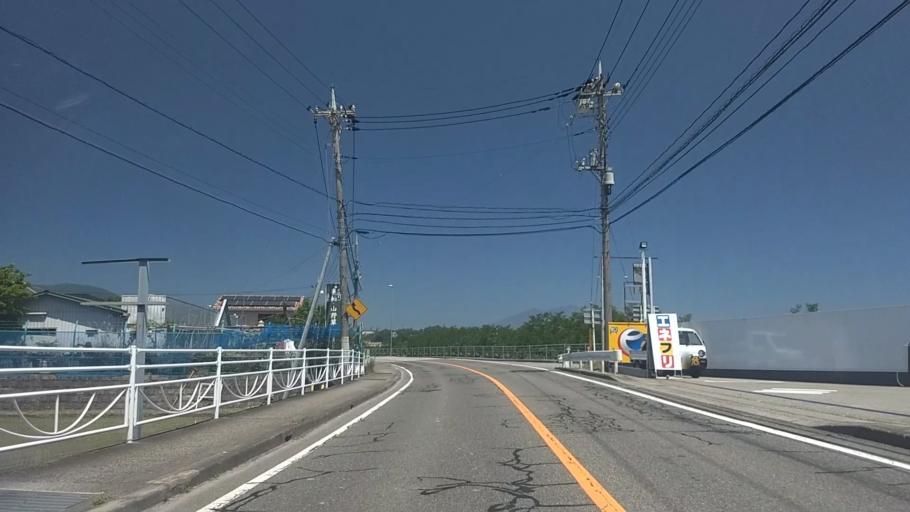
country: JP
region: Yamanashi
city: Nirasaki
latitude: 35.6966
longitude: 138.4560
